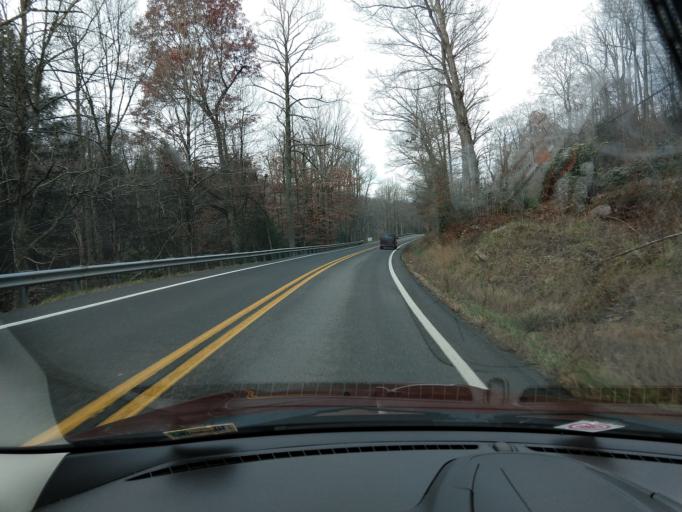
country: US
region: West Virginia
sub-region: Nicholas County
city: Summersville
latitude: 38.2614
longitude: -80.7476
